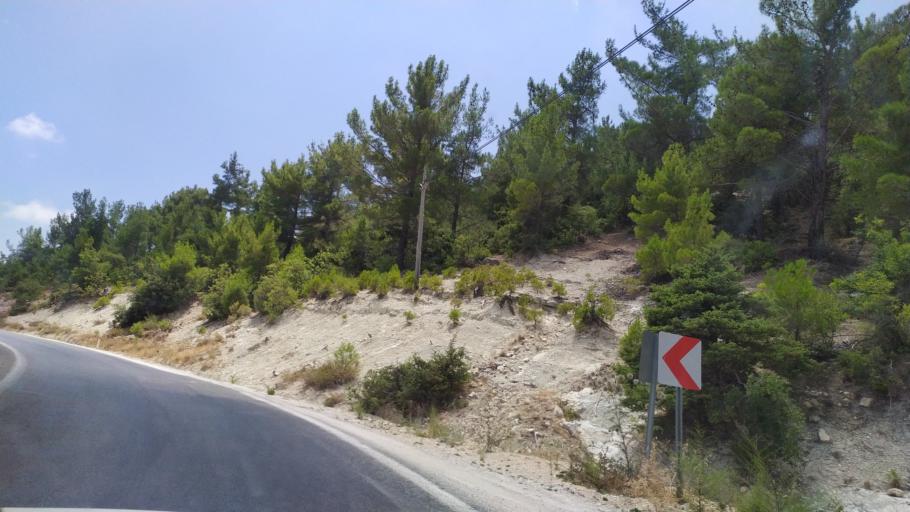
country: TR
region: Mersin
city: Gulnar
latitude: 36.2913
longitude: 33.3800
